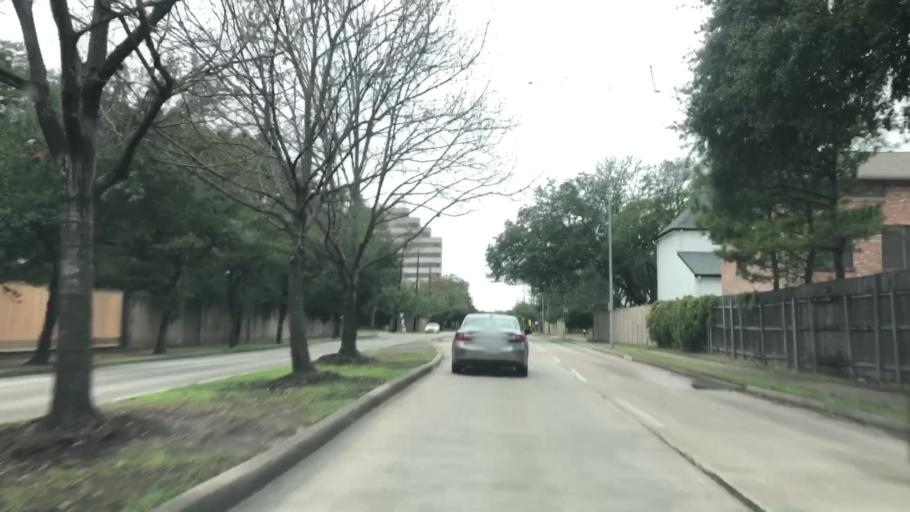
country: US
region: Texas
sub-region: Harris County
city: Hunters Creek Village
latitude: 29.7568
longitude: -95.4937
